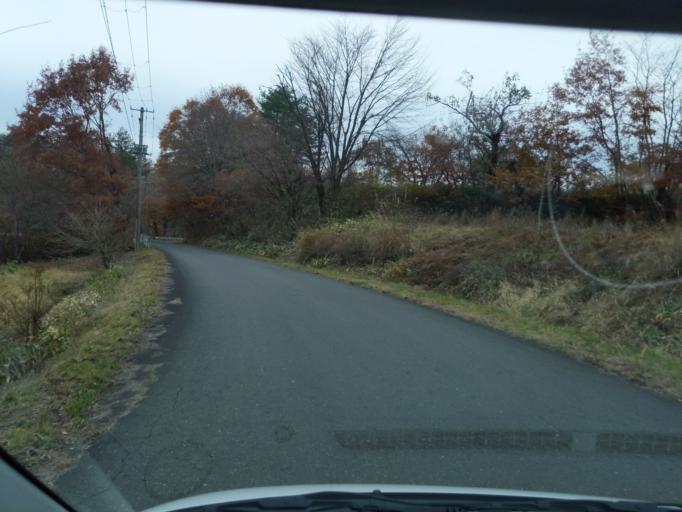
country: JP
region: Iwate
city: Ichinoseki
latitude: 38.9883
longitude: 141.0124
